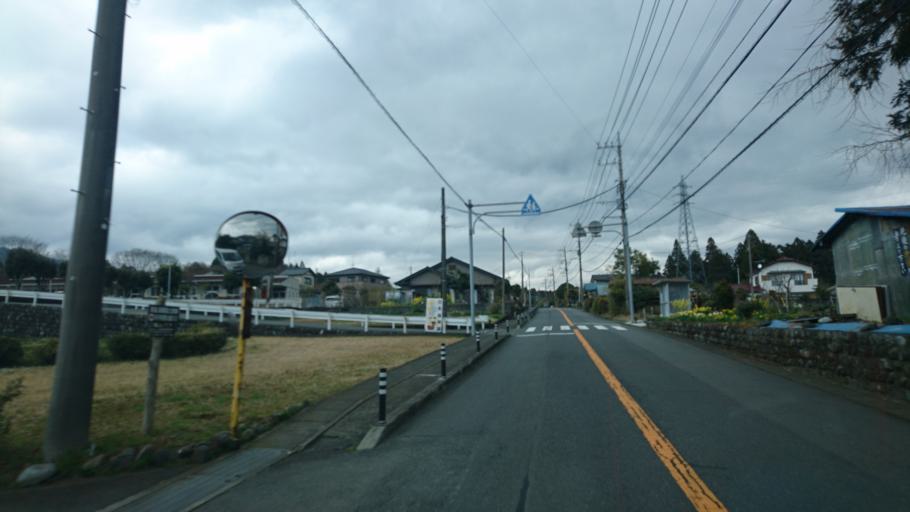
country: JP
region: Shizuoka
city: Fujinomiya
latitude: 35.3156
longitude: 138.5796
